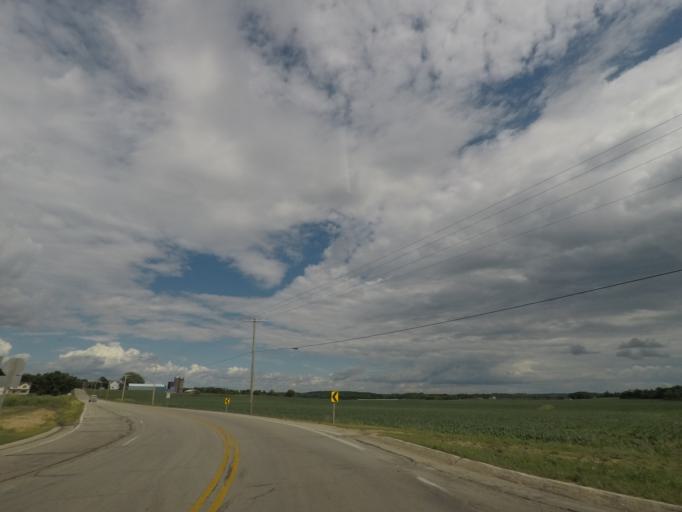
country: US
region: Wisconsin
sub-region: Dane County
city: Belleville
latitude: 42.8284
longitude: -89.5255
